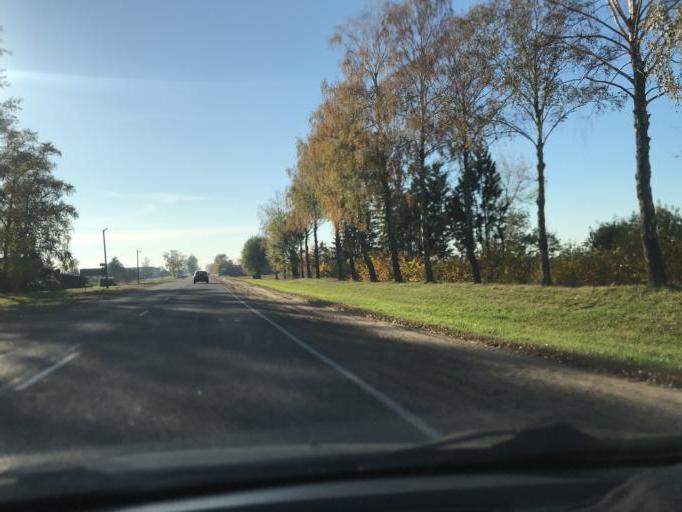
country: BY
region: Minsk
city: Slutsk
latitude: 53.0501
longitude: 27.6285
